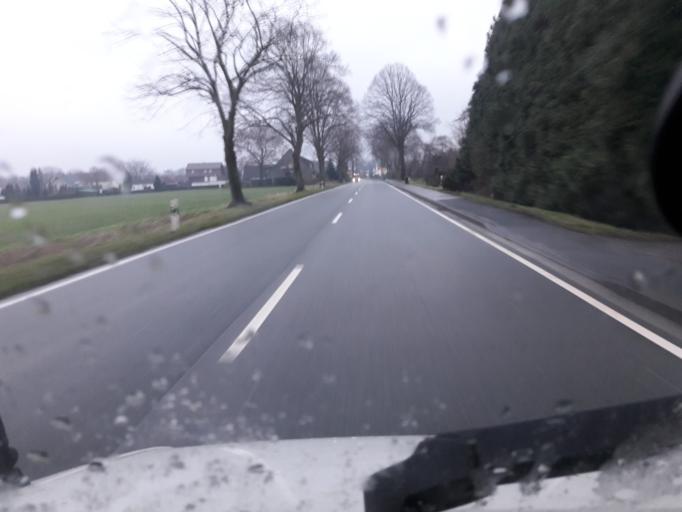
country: DE
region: North Rhine-Westphalia
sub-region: Regierungsbezirk Detmold
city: Minden
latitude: 52.2737
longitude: 8.8481
